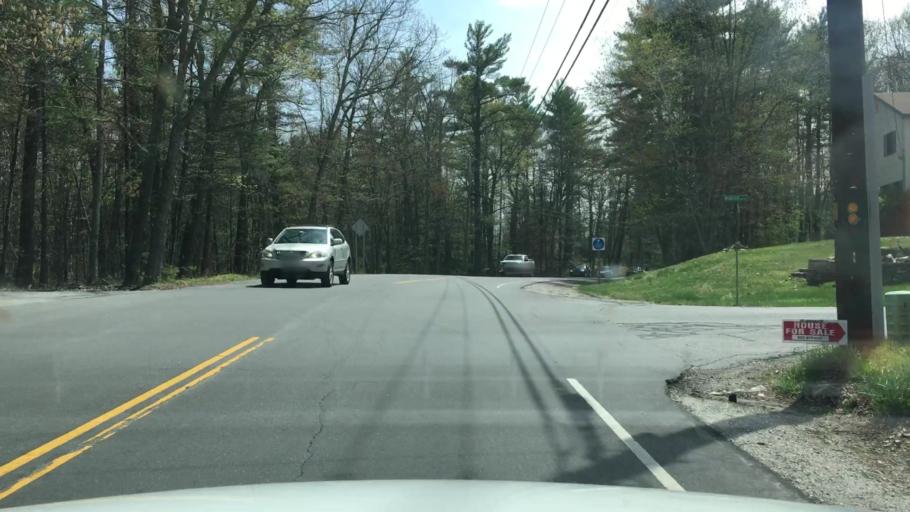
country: US
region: New Hampshire
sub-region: Rockingham County
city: Londonderry
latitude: 42.8369
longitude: -71.3621
